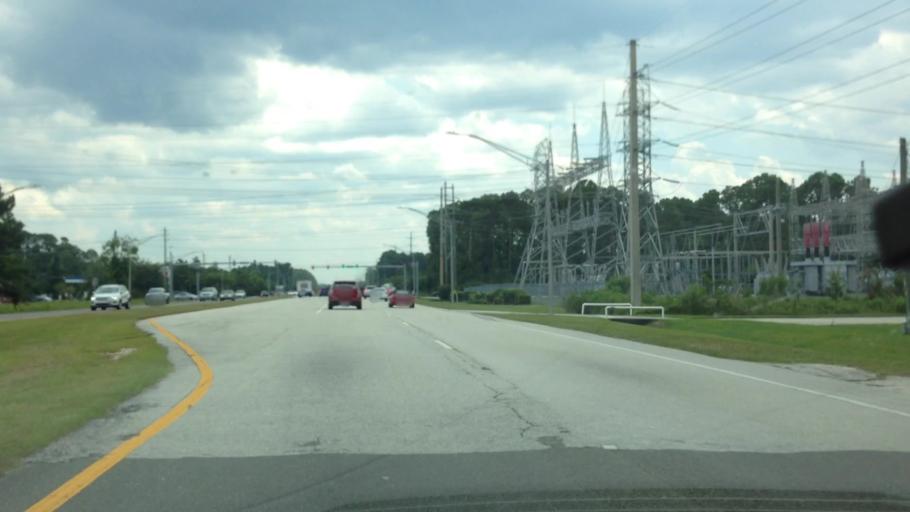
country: US
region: Florida
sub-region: Duval County
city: Neptune Beach
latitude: 30.3030
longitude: -81.5262
